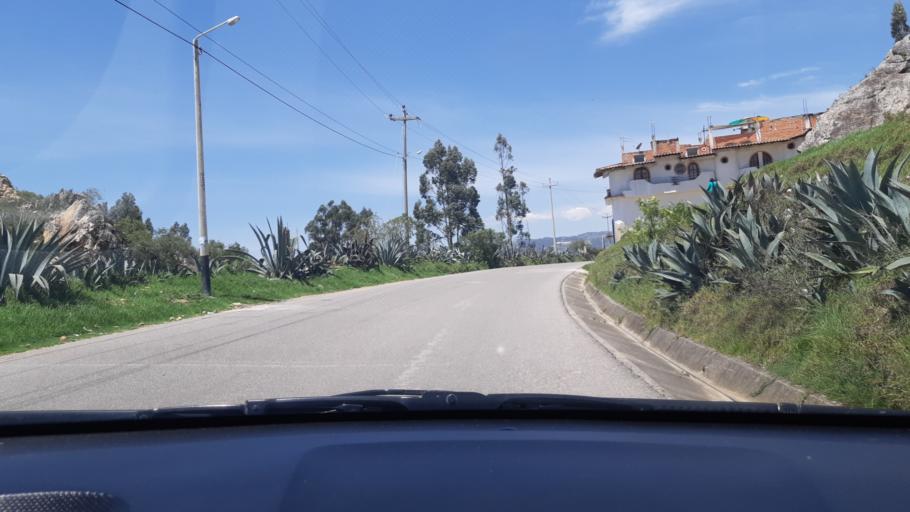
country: PE
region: Cajamarca
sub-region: Provincia de Cajamarca
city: Llacanora
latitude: -7.1746
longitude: -78.4582
